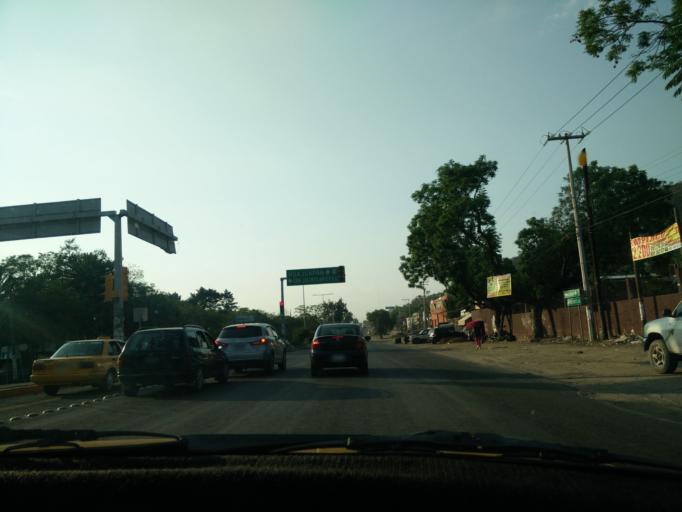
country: MX
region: Oaxaca
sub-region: Santa Maria Atzompa
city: San Jeronimo Yahuiche
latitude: 17.1033
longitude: -96.7524
